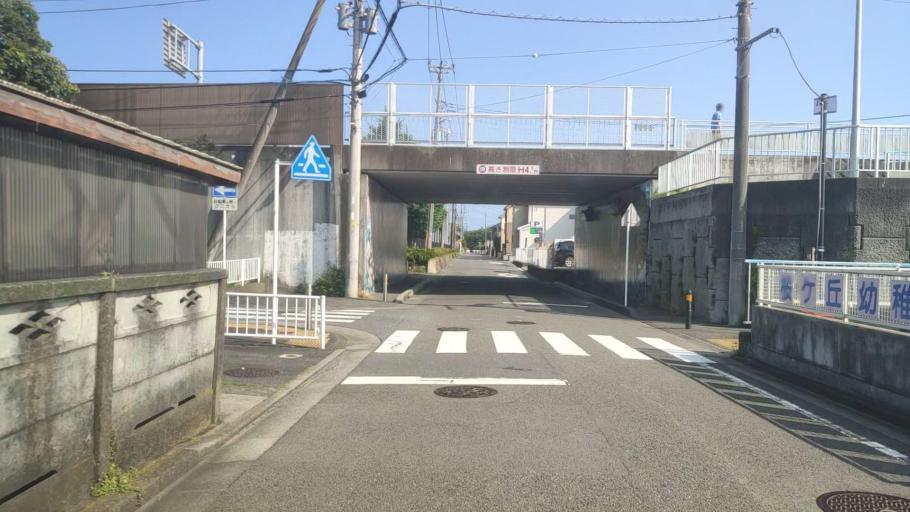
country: JP
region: Kanagawa
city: Hiratsuka
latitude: 35.3277
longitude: 139.3265
